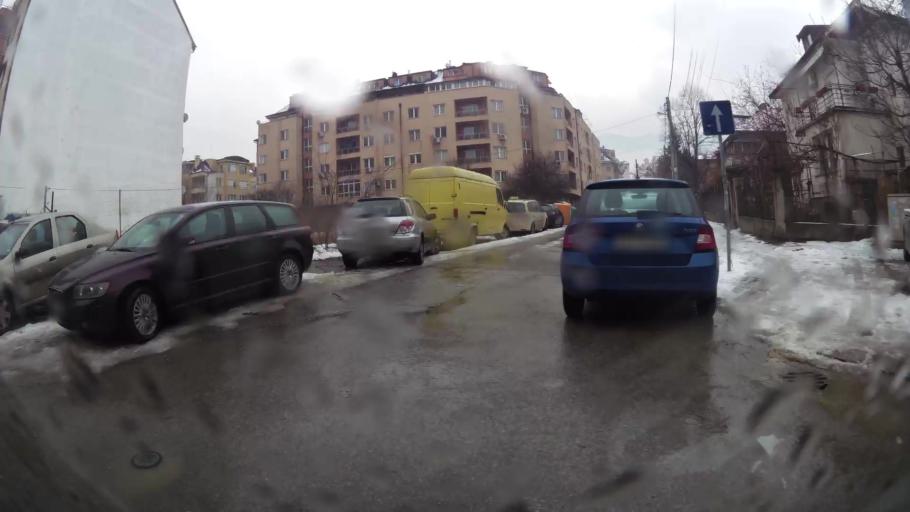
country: BG
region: Sofia-Capital
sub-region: Stolichna Obshtina
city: Sofia
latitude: 42.6629
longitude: 23.2754
